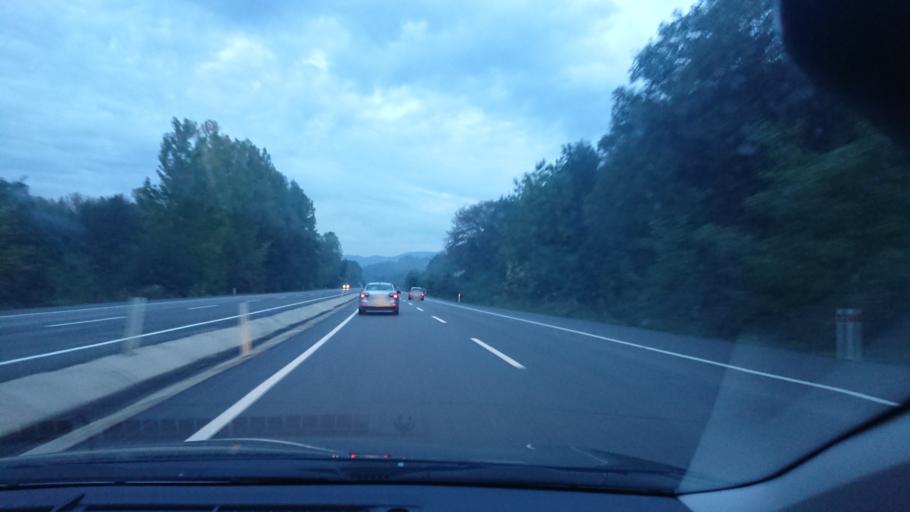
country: TR
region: Zonguldak
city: Beycuma
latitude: 41.3243
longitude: 32.0553
